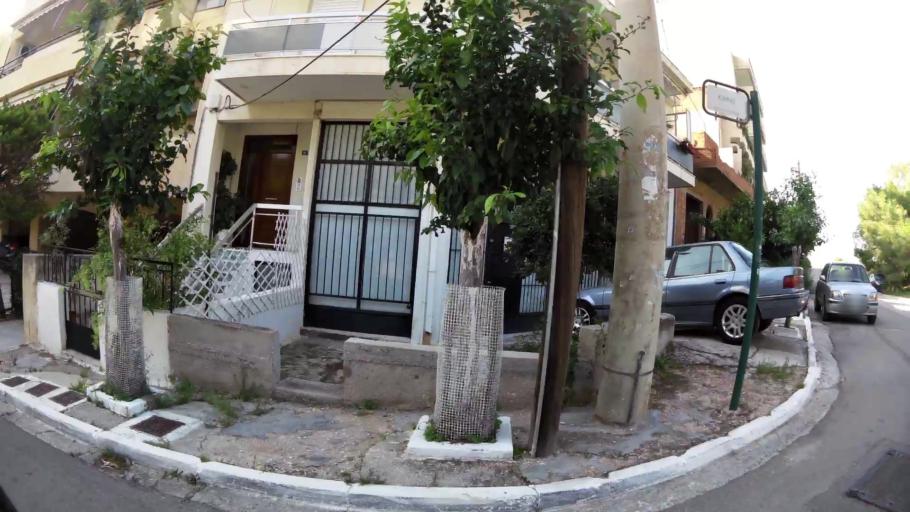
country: GR
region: Attica
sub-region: Nomarchia Athinas
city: Argyroupoli
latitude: 37.9103
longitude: 23.7592
